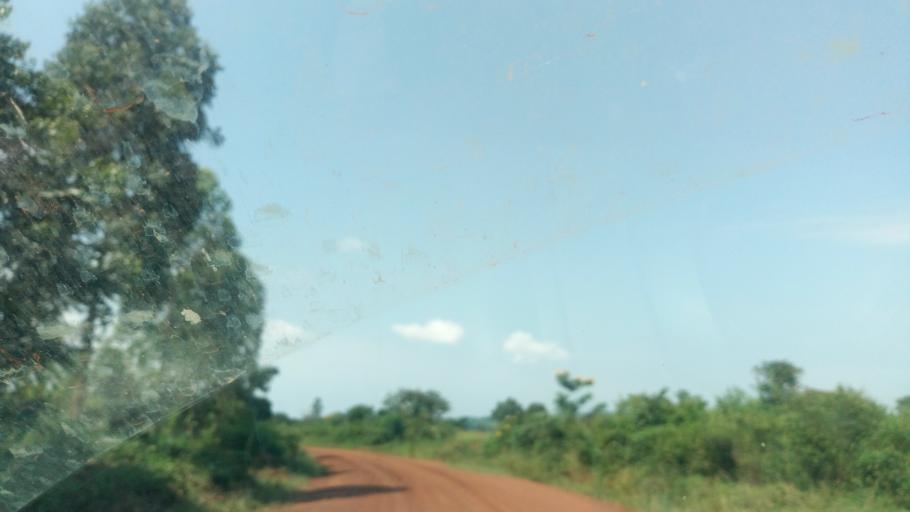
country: UG
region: Western Region
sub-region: Masindi District
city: Masindi
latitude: 1.6790
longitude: 31.8300
